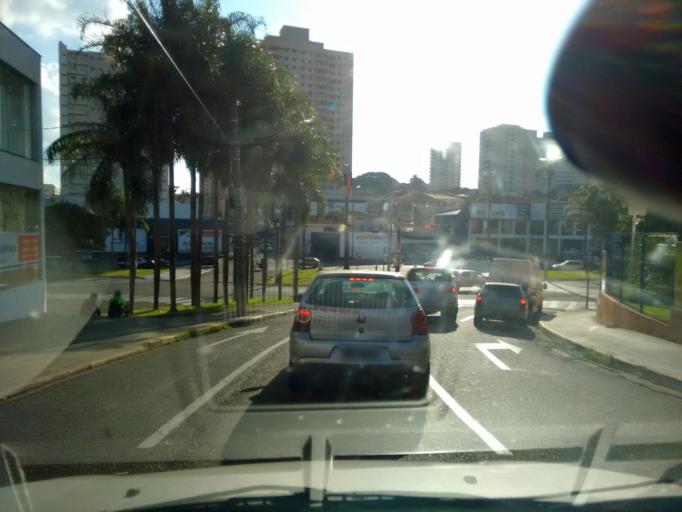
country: BR
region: Sao Paulo
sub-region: Araraquara
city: Araraquara
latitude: -21.7971
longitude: -48.1723
